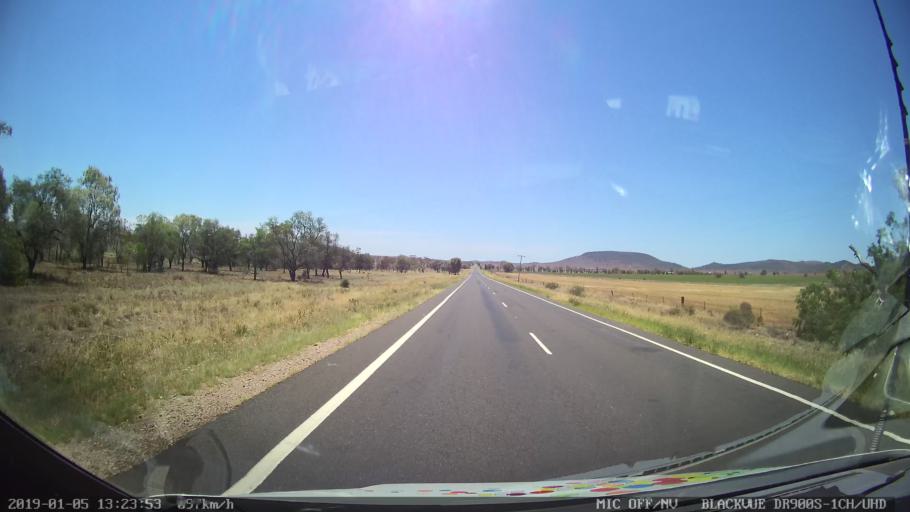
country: AU
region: New South Wales
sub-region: Gunnedah
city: Gunnedah
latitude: -31.0742
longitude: 149.9813
